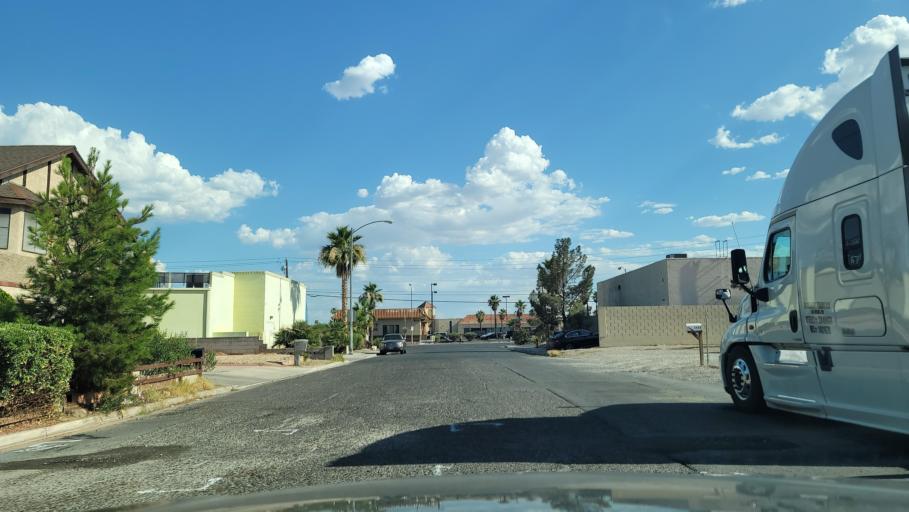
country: US
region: Nevada
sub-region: Clark County
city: Spring Valley
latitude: 36.1272
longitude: -115.2055
